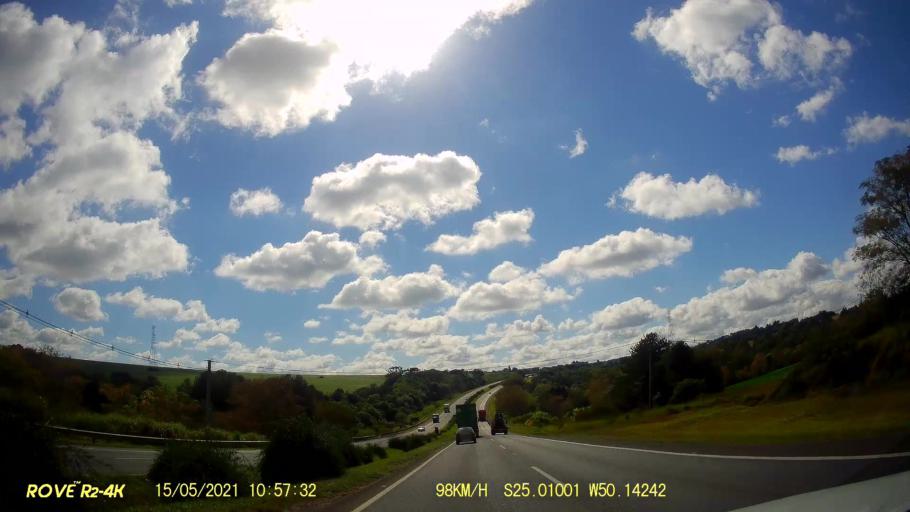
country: BR
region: Parana
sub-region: Carambei
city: Carambei
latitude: -25.0102
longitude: -50.1426
